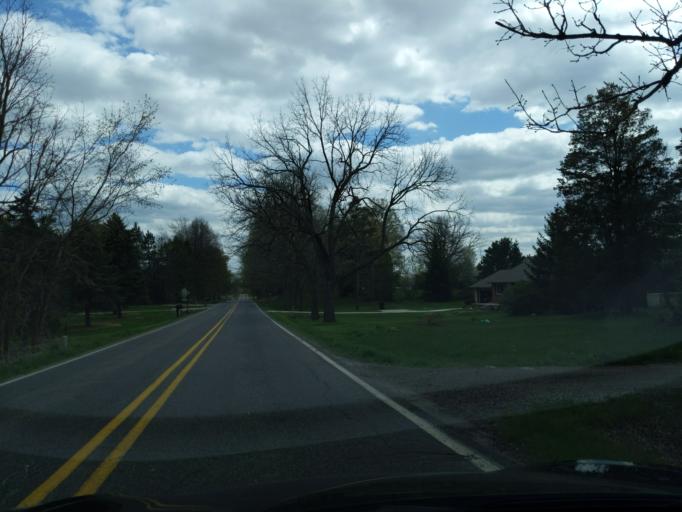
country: US
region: Michigan
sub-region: Ingham County
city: Holt
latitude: 42.6394
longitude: -84.4626
